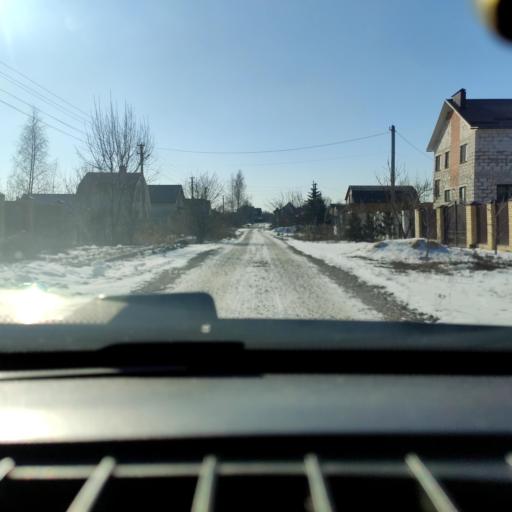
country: RU
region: Voronezj
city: Novaya Usman'
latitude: 51.6659
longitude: 39.3347
